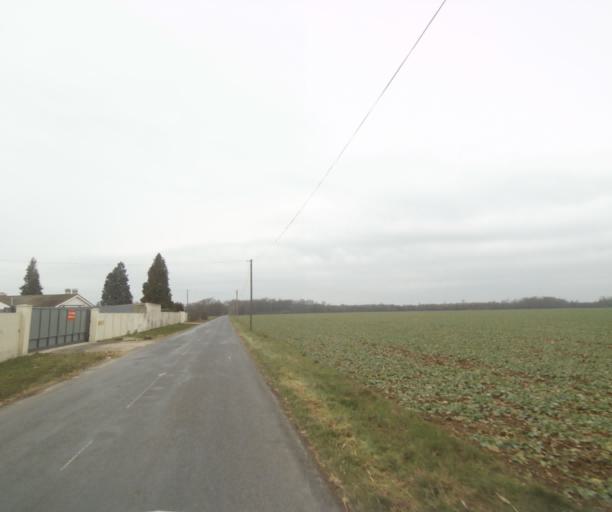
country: FR
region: Champagne-Ardenne
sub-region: Departement de la Haute-Marne
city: Villiers-en-Lieu
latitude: 48.6618
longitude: 4.8857
